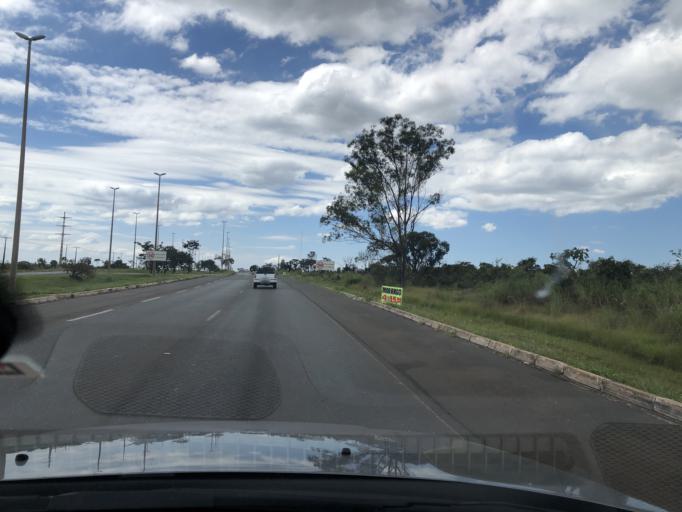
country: BR
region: Federal District
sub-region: Brasilia
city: Brasilia
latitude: -15.9783
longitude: -47.9979
